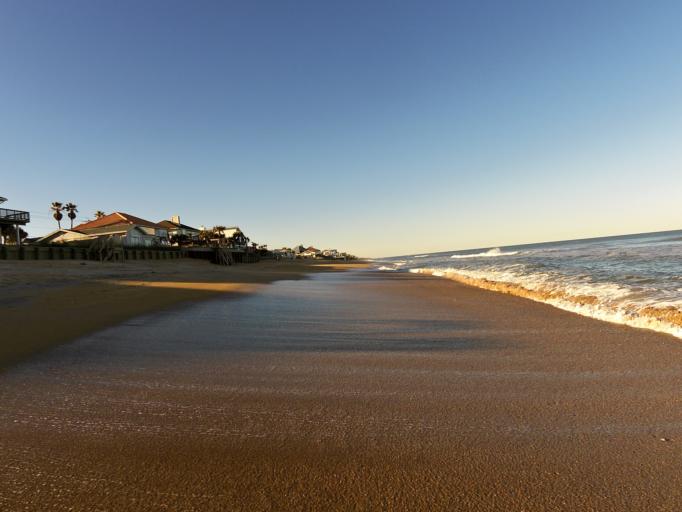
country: US
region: Florida
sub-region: Saint Johns County
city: Villano Beach
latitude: 30.0015
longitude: -81.3173
